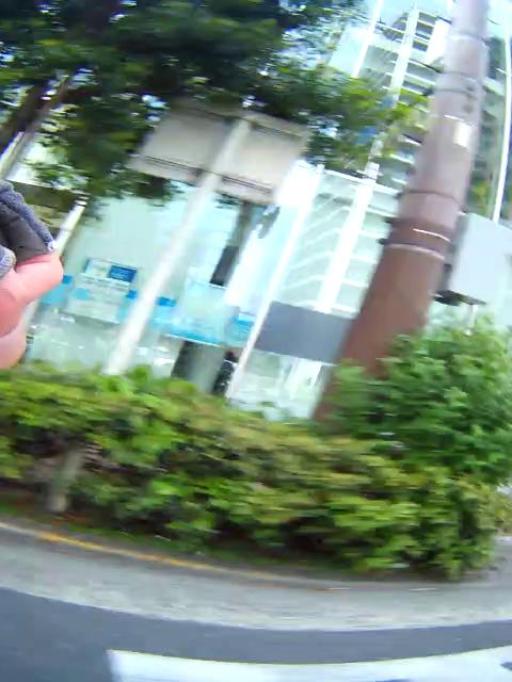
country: JP
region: Osaka
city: Osaka-shi
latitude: 34.6658
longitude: 135.5424
